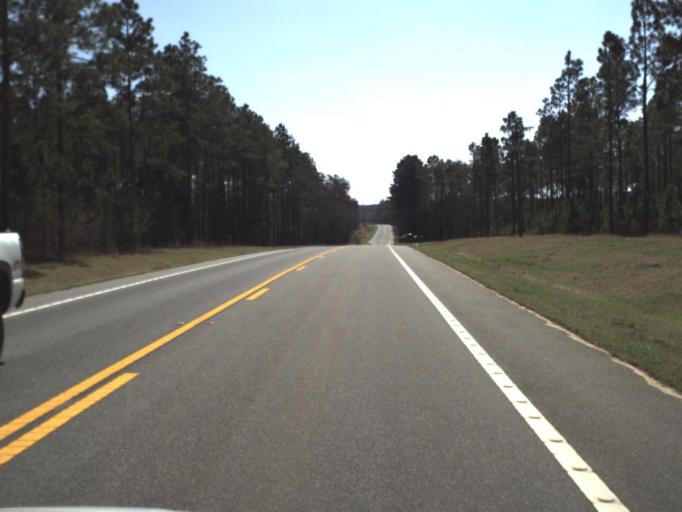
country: US
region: Florida
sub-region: Jackson County
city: Sneads
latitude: 30.6167
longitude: -85.0296
